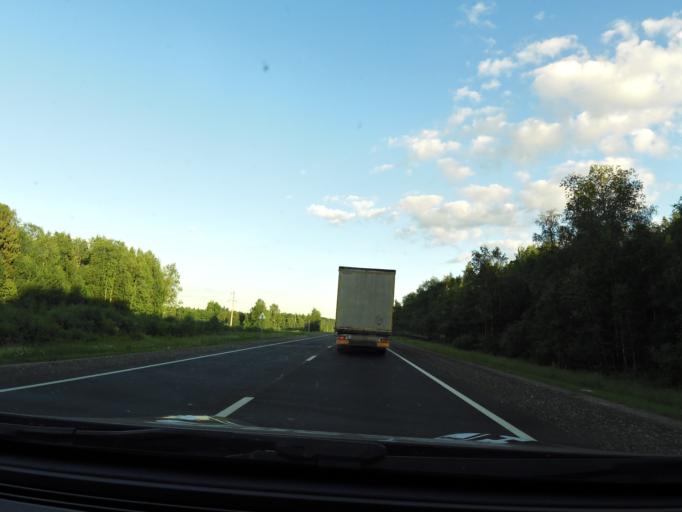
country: RU
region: Vologda
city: Gryazovets
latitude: 58.9875
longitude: 40.1394
